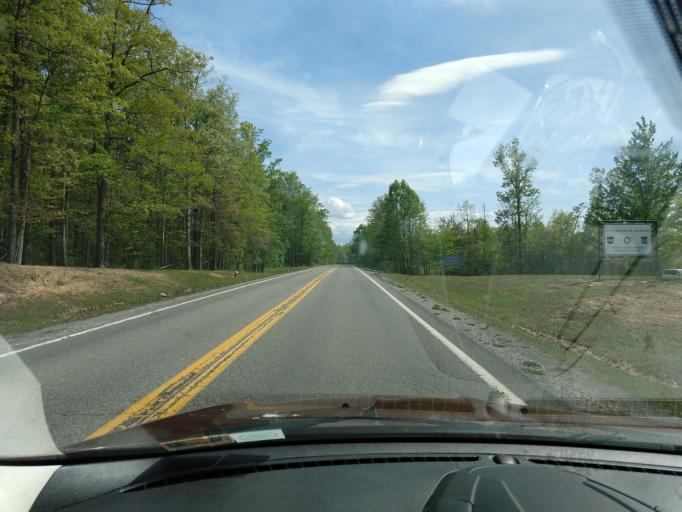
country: US
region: West Virginia
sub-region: Raleigh County
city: Stanaford
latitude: 37.7884
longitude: -81.1166
